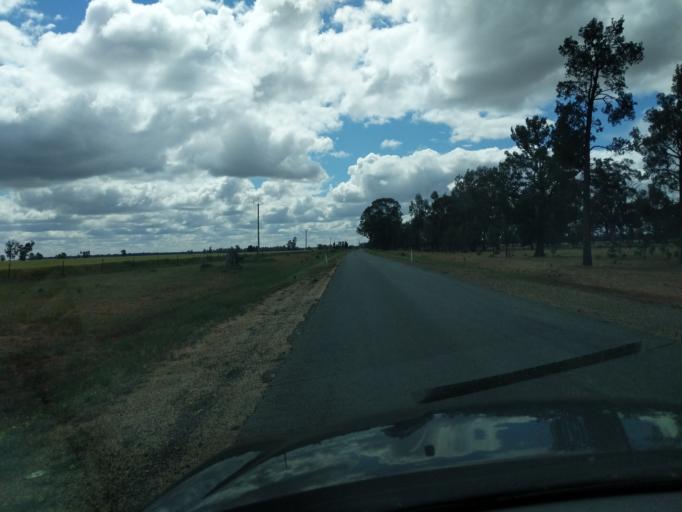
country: AU
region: New South Wales
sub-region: Coolamon
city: Coolamon
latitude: -34.8648
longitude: 146.8970
